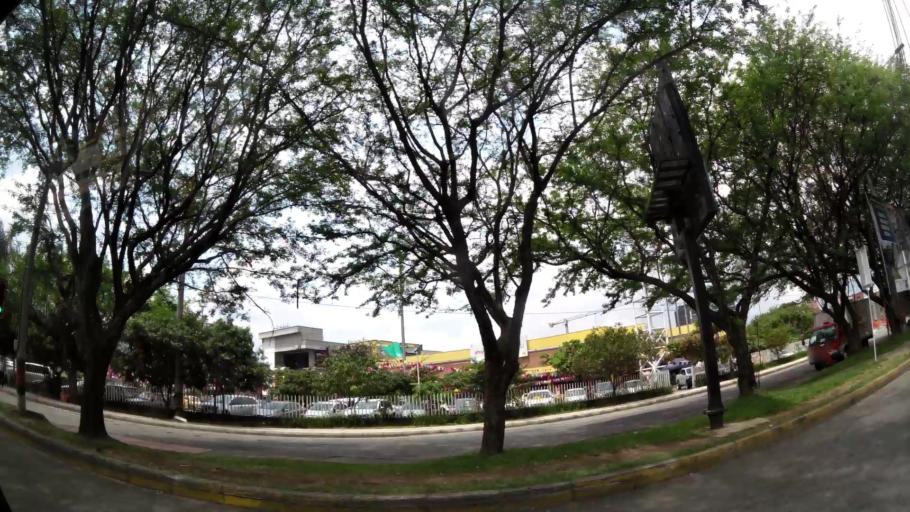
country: CO
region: Antioquia
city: Envigado
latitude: 6.1740
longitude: -75.5927
